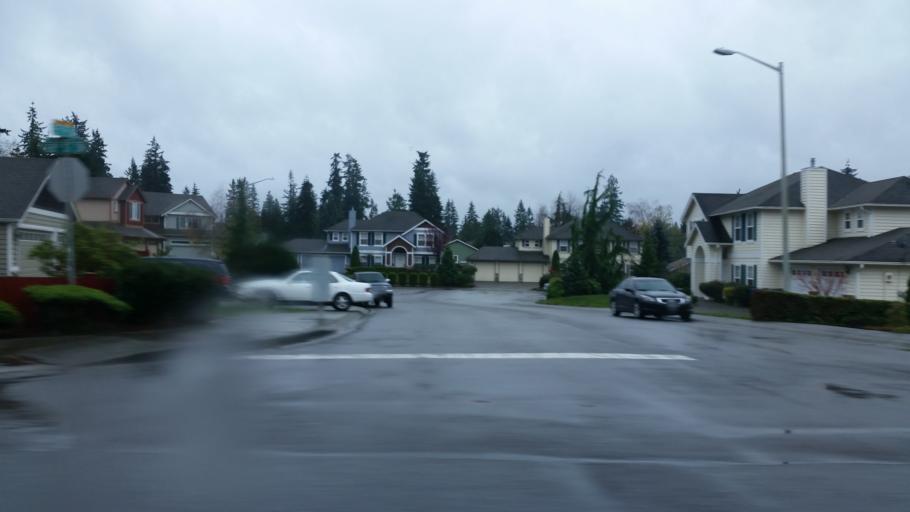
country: US
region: Washington
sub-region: Snohomish County
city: Lynnwood
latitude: 47.8466
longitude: -122.3073
